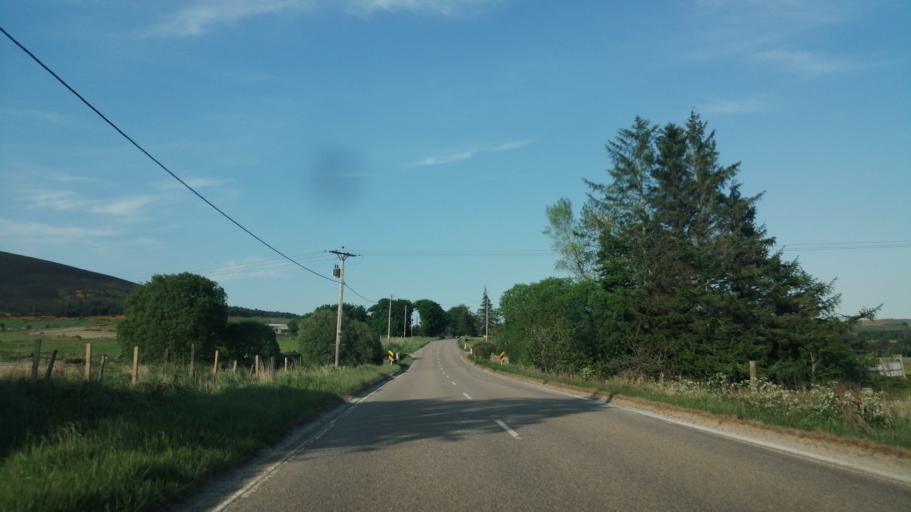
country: GB
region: Scotland
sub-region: Aberdeenshire
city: Huntly
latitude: 57.5660
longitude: -2.7896
